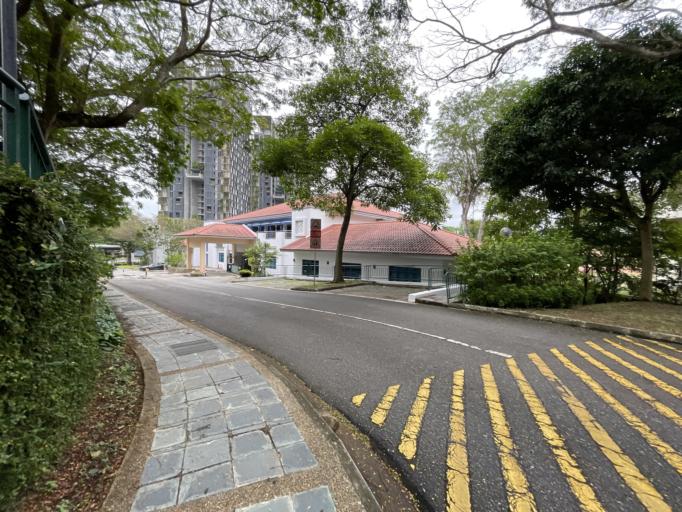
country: SG
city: Singapore
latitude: 1.3012
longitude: 103.7687
